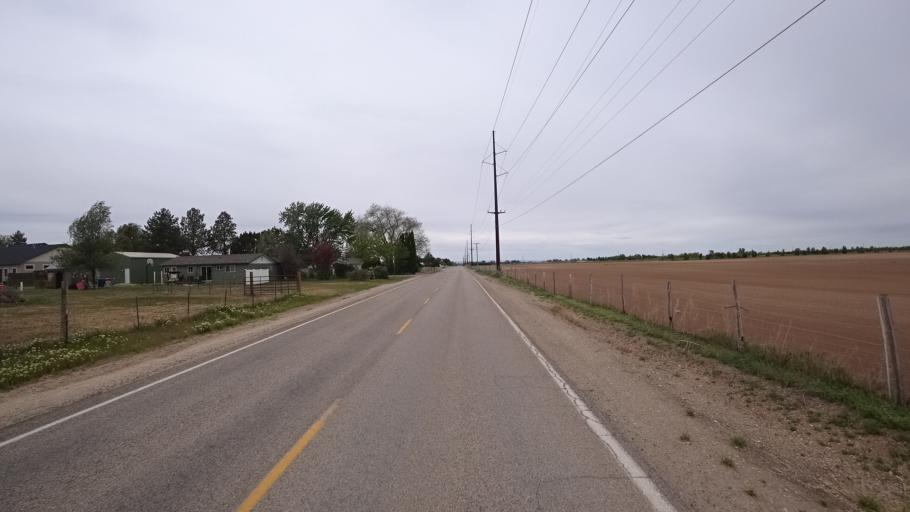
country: US
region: Idaho
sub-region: Ada County
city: Kuna
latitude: 43.4882
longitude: -116.3185
